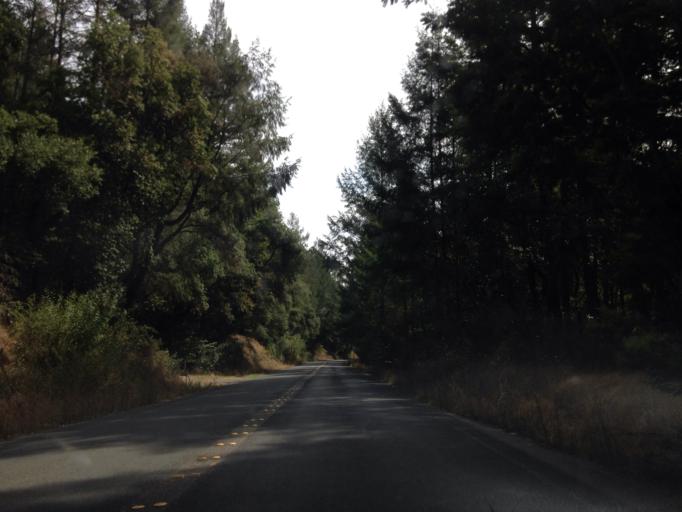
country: US
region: California
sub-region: Sonoma County
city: Occidental
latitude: 38.4151
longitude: -122.9306
